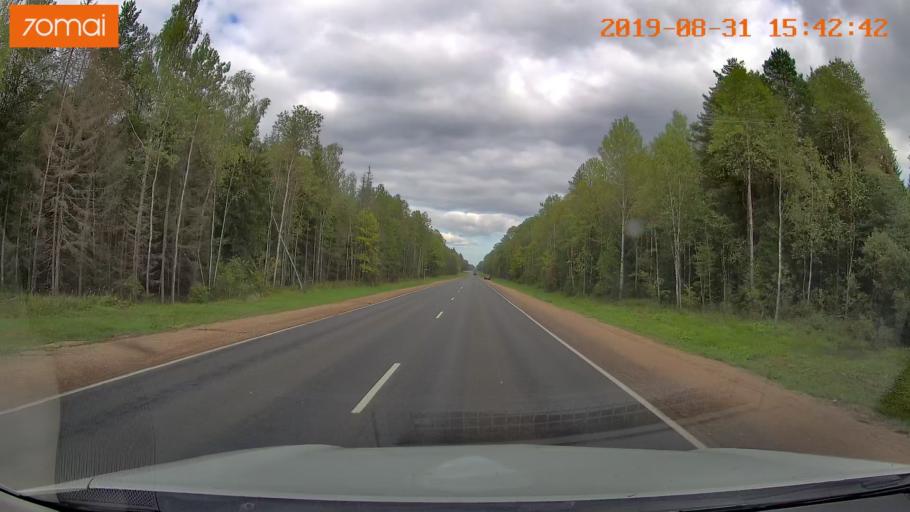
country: RU
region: Kaluga
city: Mosal'sk
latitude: 54.6481
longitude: 34.8928
